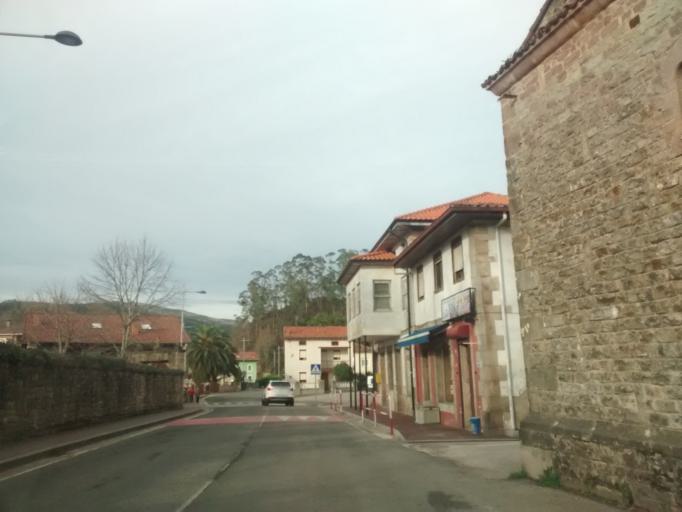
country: ES
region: Cantabria
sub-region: Provincia de Cantabria
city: Luzmela
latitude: 43.3189
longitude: -4.1912
